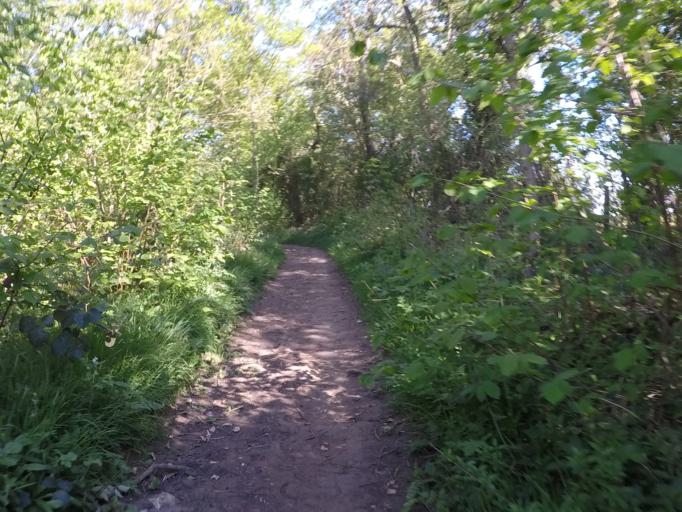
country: GB
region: England
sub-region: Oxfordshire
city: Charlbury
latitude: 51.8612
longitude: -1.4655
